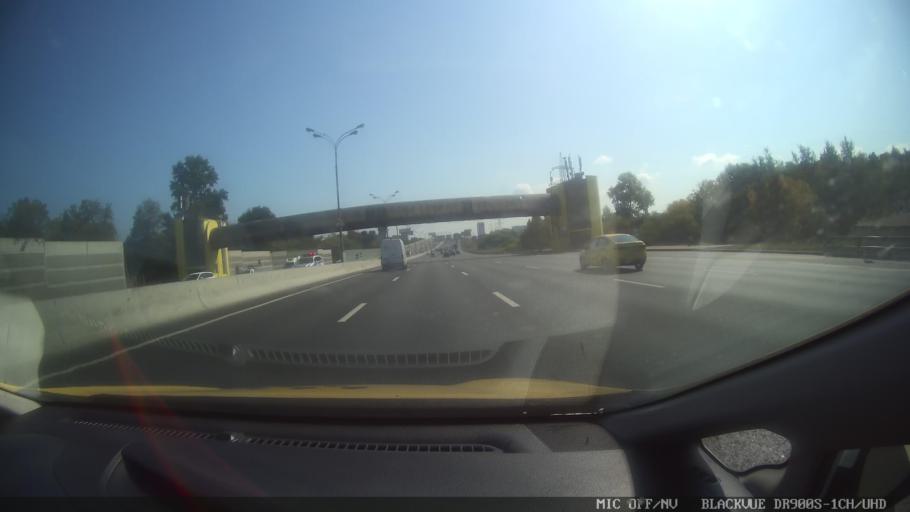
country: RU
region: Moscow
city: Yaroslavskiy
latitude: 55.8927
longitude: 37.7051
